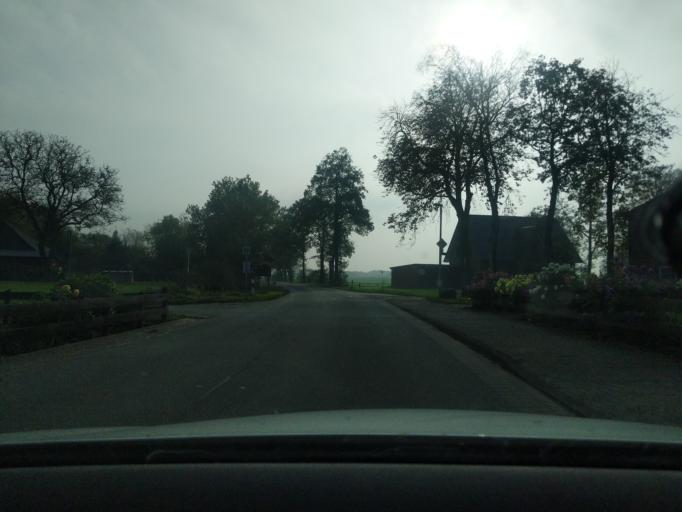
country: DE
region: Lower Saxony
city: Wanna
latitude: 53.7375
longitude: 8.7868
